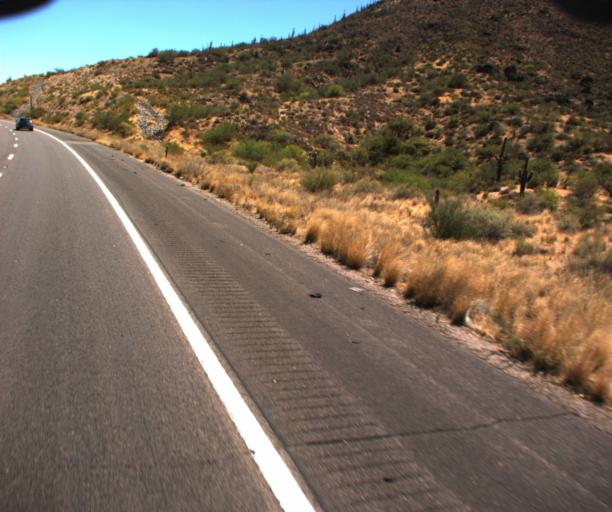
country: US
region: Arizona
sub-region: Maricopa County
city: Rio Verde
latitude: 33.7917
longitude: -111.4951
